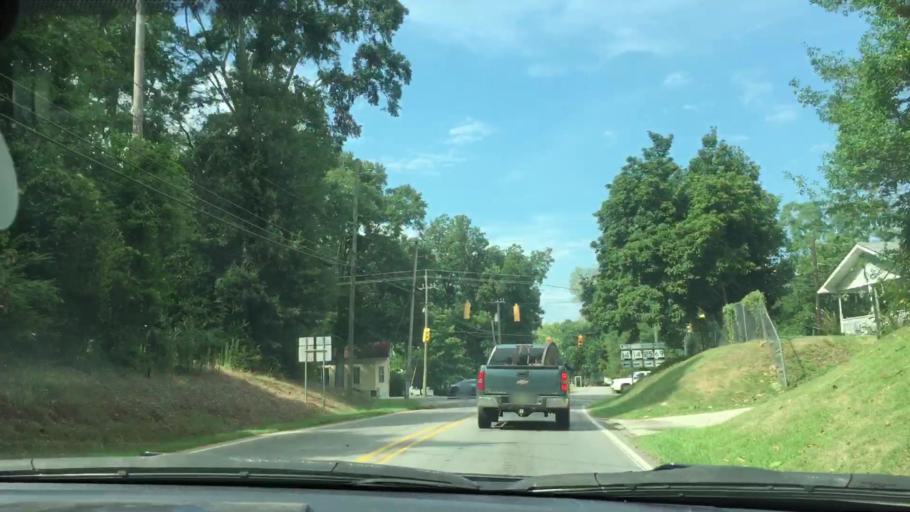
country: US
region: Alabama
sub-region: Hale County
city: Greensboro
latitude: 32.6997
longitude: -87.6004
